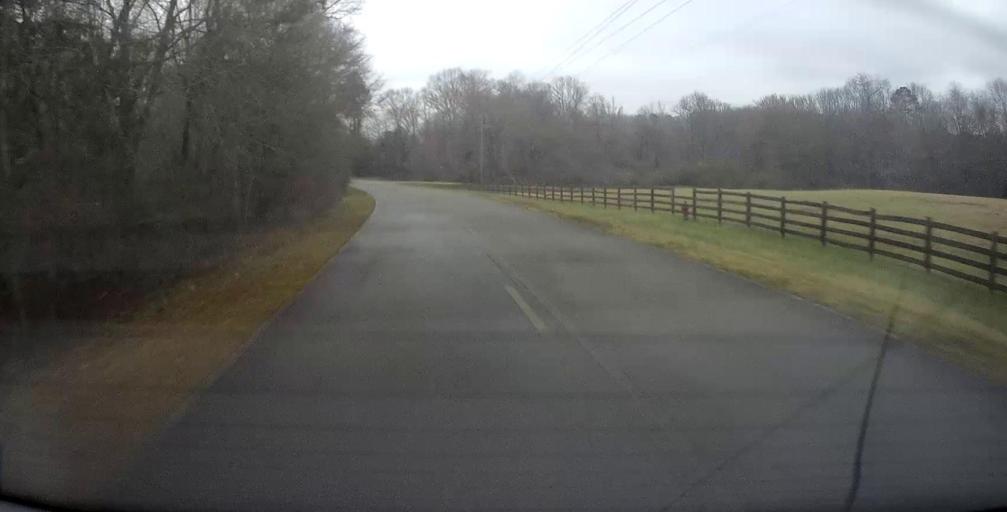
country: US
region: Georgia
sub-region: Lamar County
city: Barnesville
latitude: 33.0289
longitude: -84.1115
